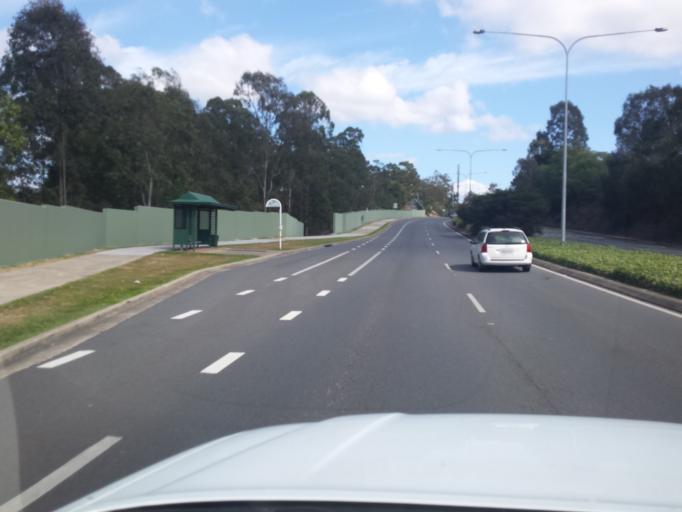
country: AU
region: Queensland
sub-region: Brisbane
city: Bridegman Downs
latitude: -27.3662
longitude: 152.9762
